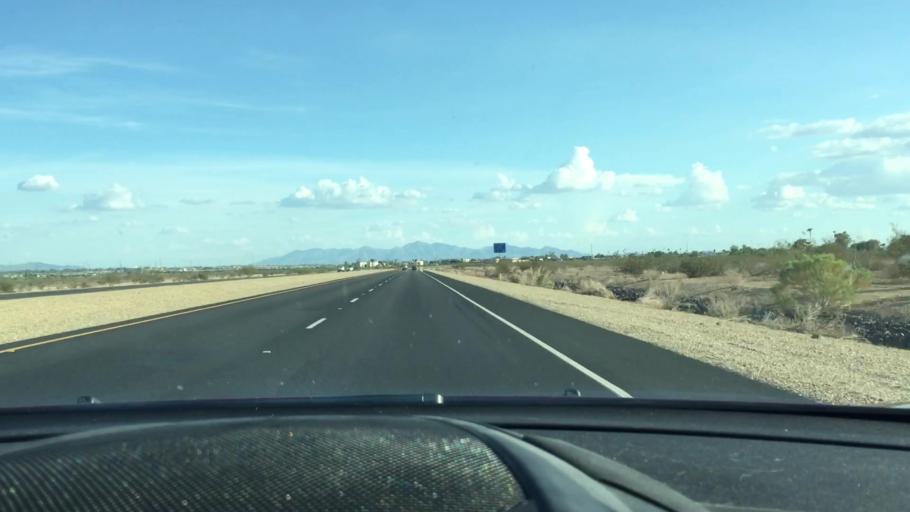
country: US
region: Arizona
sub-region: Maricopa County
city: Sun City West
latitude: 33.6545
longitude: -112.3234
